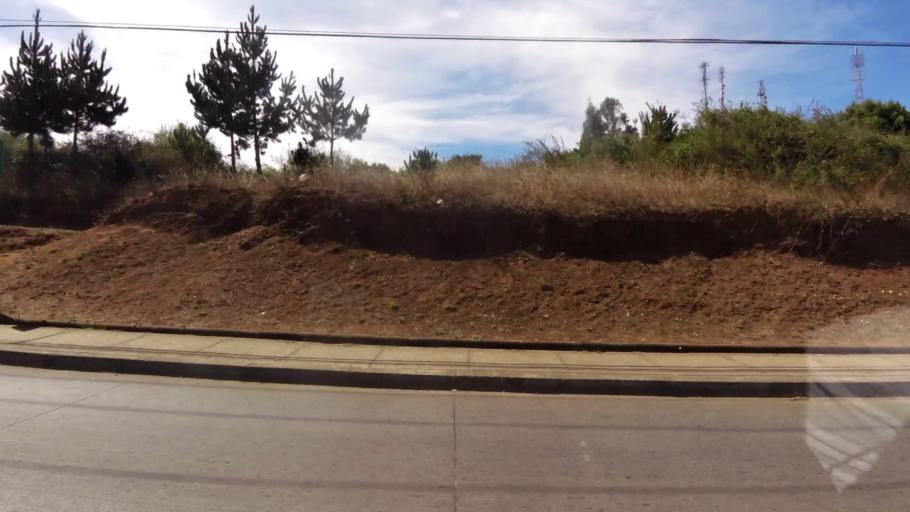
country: CL
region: Biobio
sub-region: Provincia de Concepcion
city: Talcahuano
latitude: -36.7095
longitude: -73.1296
